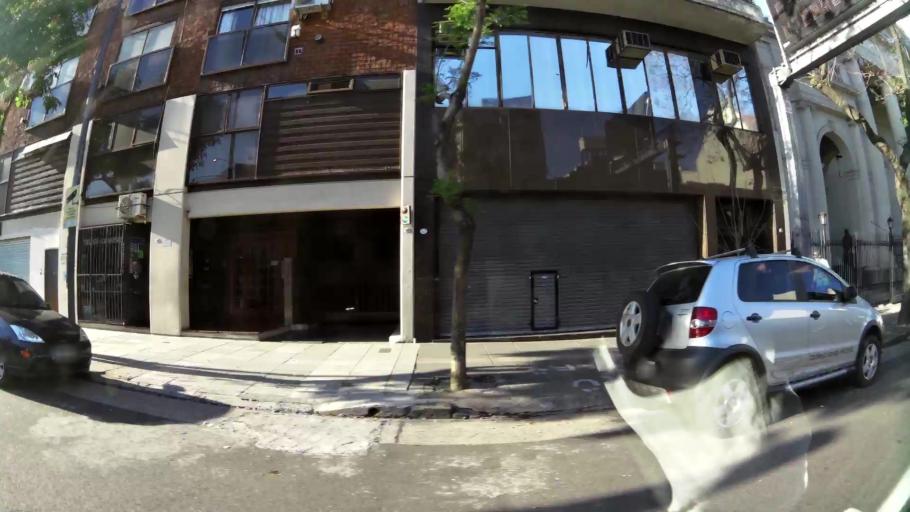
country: AR
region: Buenos Aires F.D.
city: Buenos Aires
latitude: -34.6131
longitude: -58.3829
